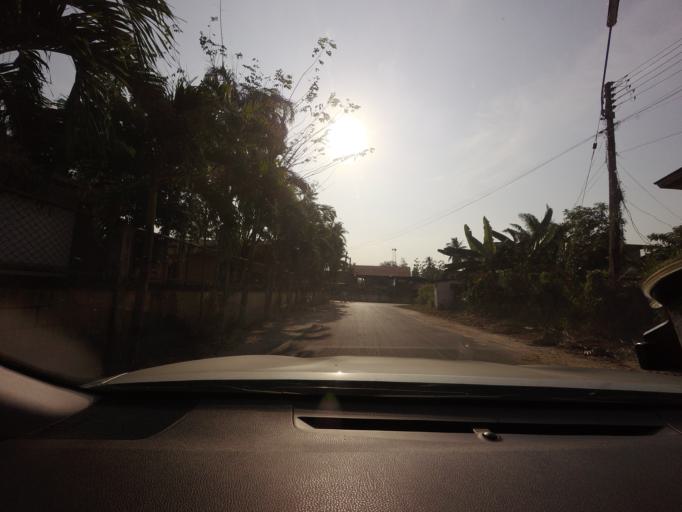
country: TH
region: Narathiwat
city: Rueso
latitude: 6.3999
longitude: 101.5235
